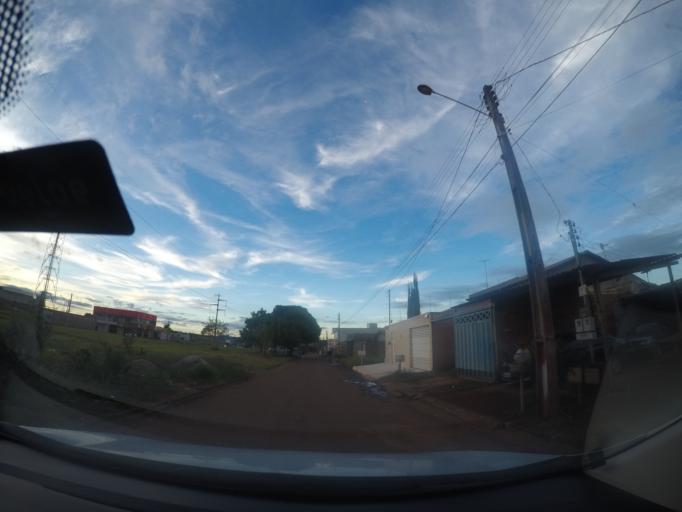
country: BR
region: Goias
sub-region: Goianira
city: Goianira
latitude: -16.5738
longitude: -49.3813
